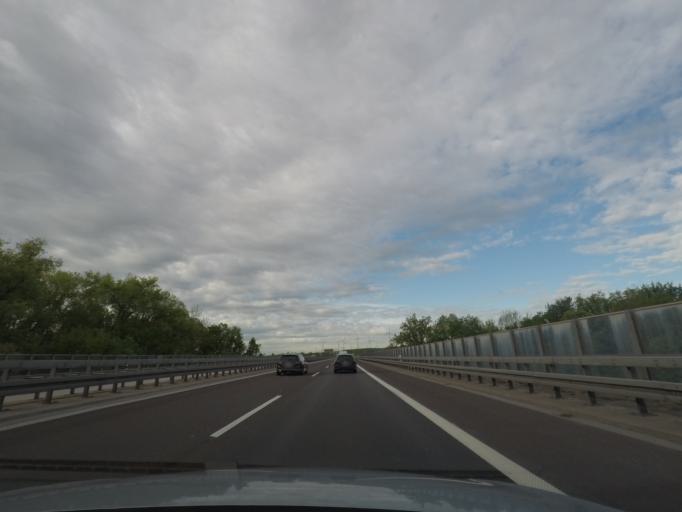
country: DE
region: Saxony-Anhalt
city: Ilberstedt
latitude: 51.7948
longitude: 11.6779
